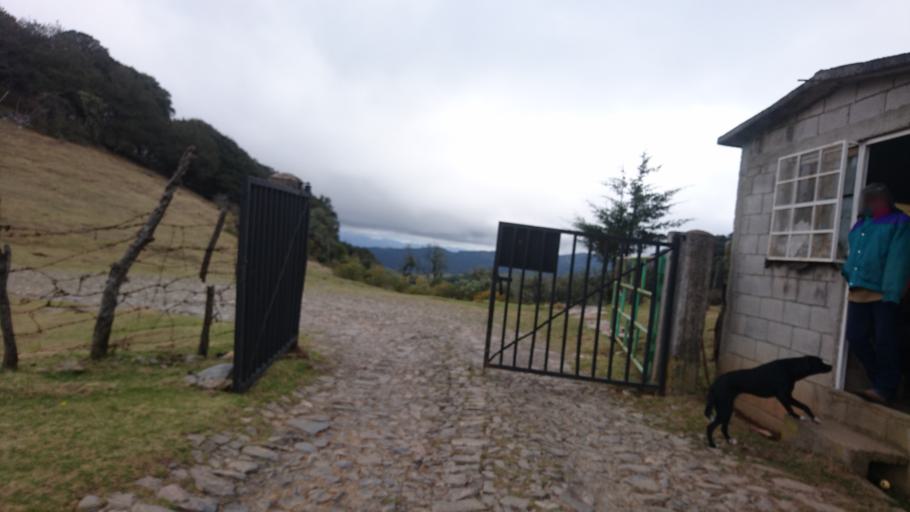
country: MX
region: San Luis Potosi
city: Zaragoza
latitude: 22.0726
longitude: -100.6380
